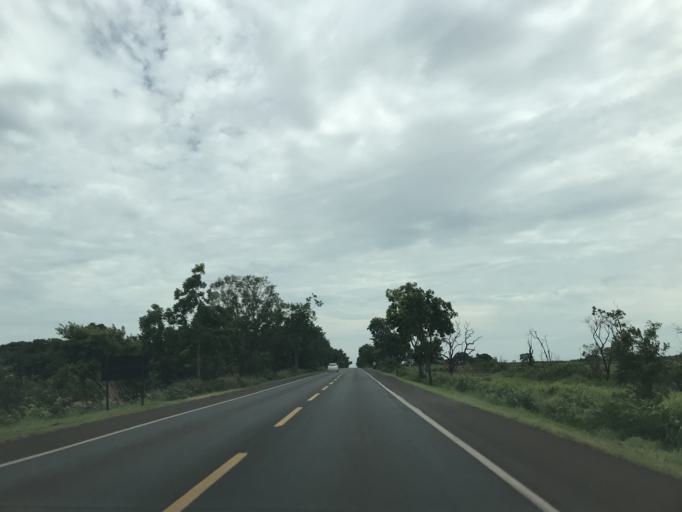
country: BR
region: Minas Gerais
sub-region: Frutal
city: Frutal
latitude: -20.1725
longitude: -49.1136
